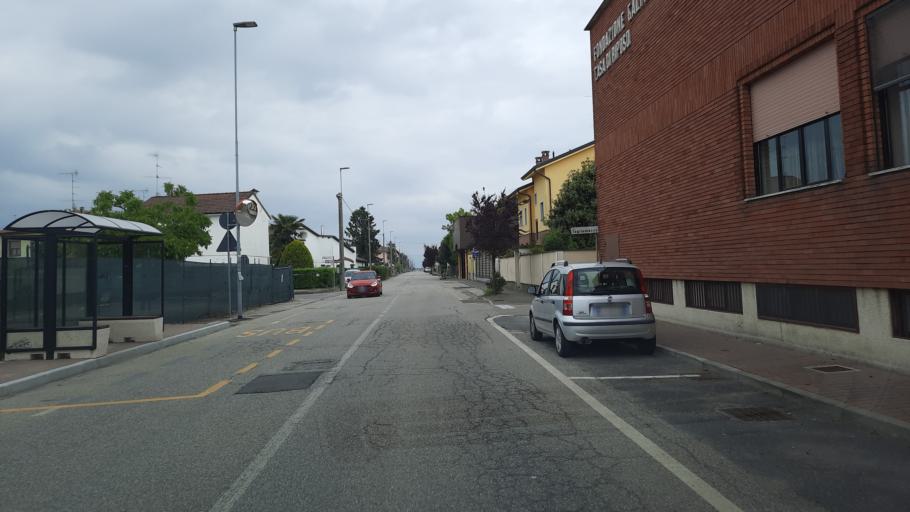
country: IT
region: Lombardy
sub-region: Provincia di Pavia
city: Robbio
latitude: 45.2864
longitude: 8.5964
